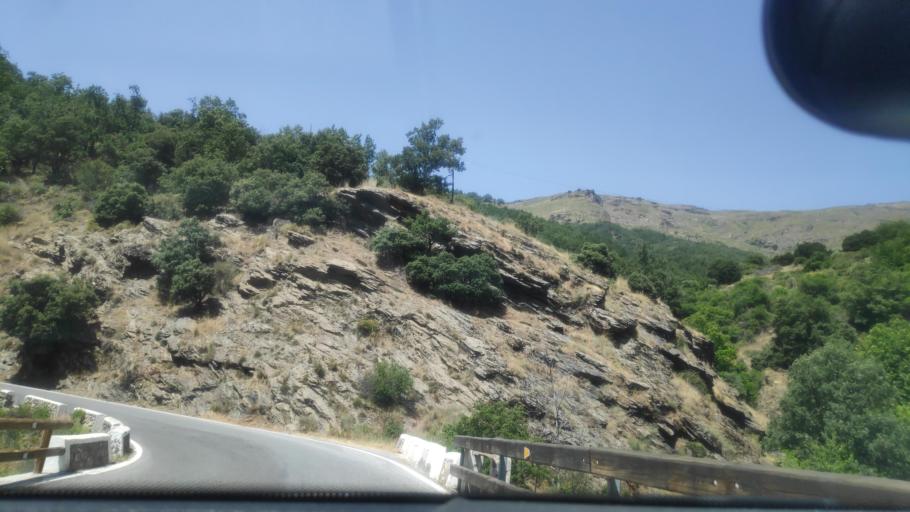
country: ES
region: Andalusia
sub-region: Provincia de Granada
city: Trevelez
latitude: 36.9837
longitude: -3.2799
